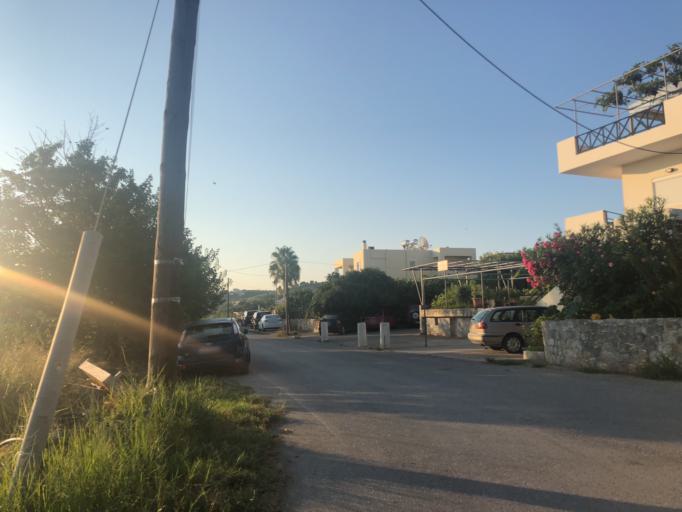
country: GR
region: Crete
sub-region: Nomos Chanias
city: Georgioupolis
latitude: 35.3457
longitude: 24.3011
